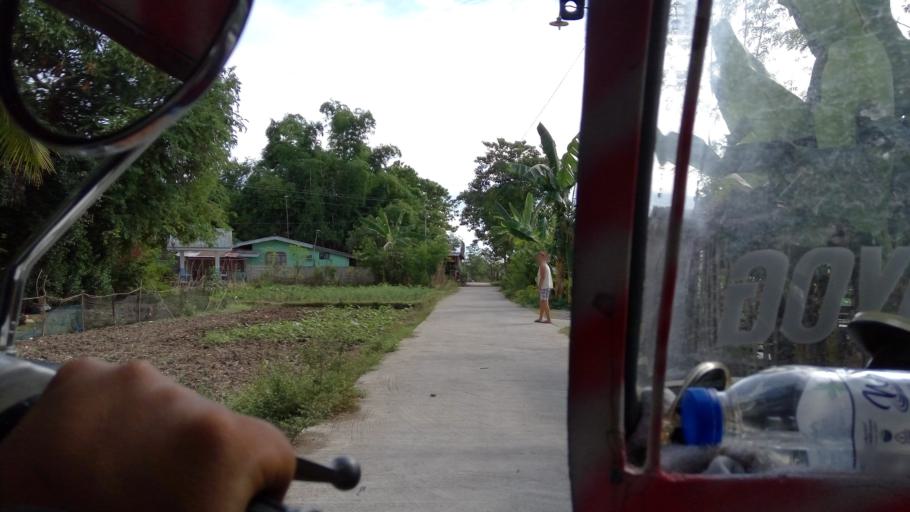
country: PH
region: Ilocos
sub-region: Province of La Union
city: San Eugenio
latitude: 16.3657
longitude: 120.3525
